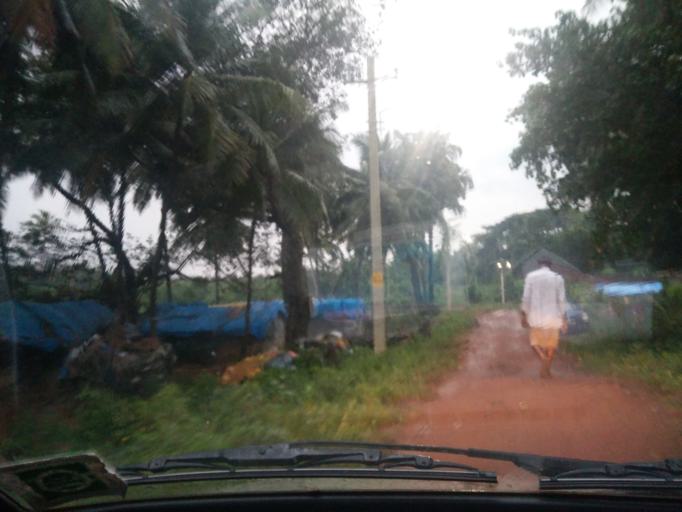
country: IN
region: Goa
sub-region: South Goa
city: Madgaon
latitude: 15.2877
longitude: 73.9433
